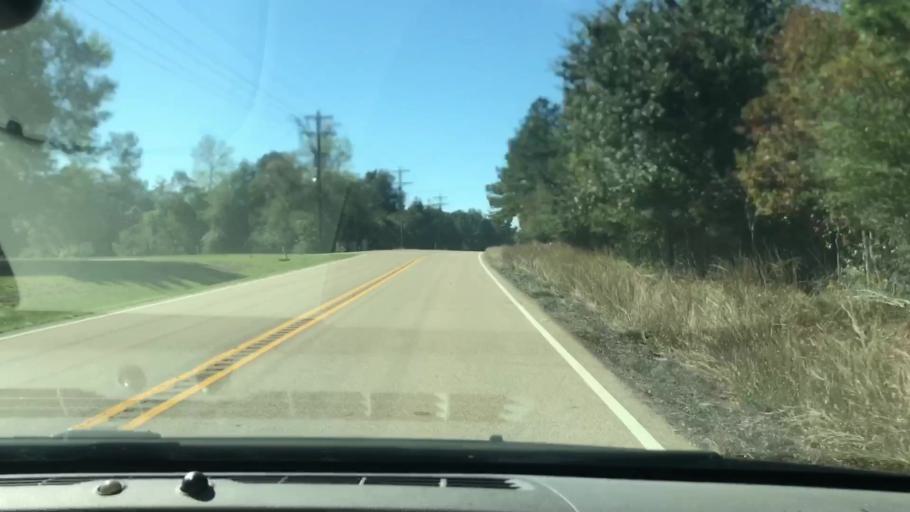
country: US
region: Louisiana
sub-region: Saint Tammany Parish
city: Abita Springs
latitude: 30.5185
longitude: -89.9379
